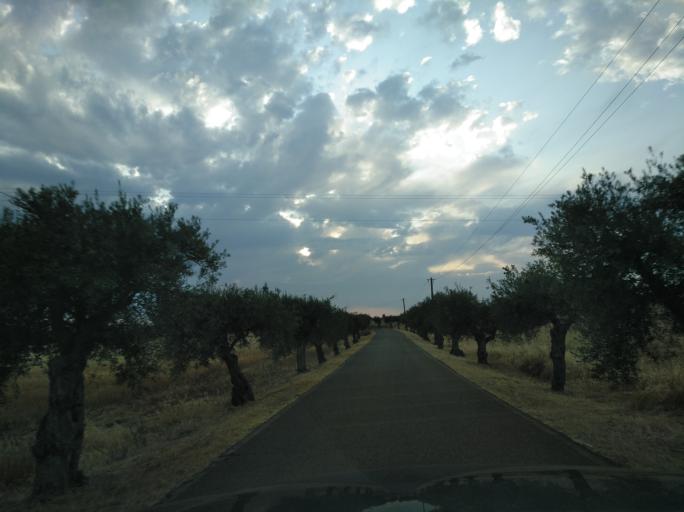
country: PT
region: Portalegre
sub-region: Campo Maior
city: Campo Maior
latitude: 39.0161
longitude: -7.0351
